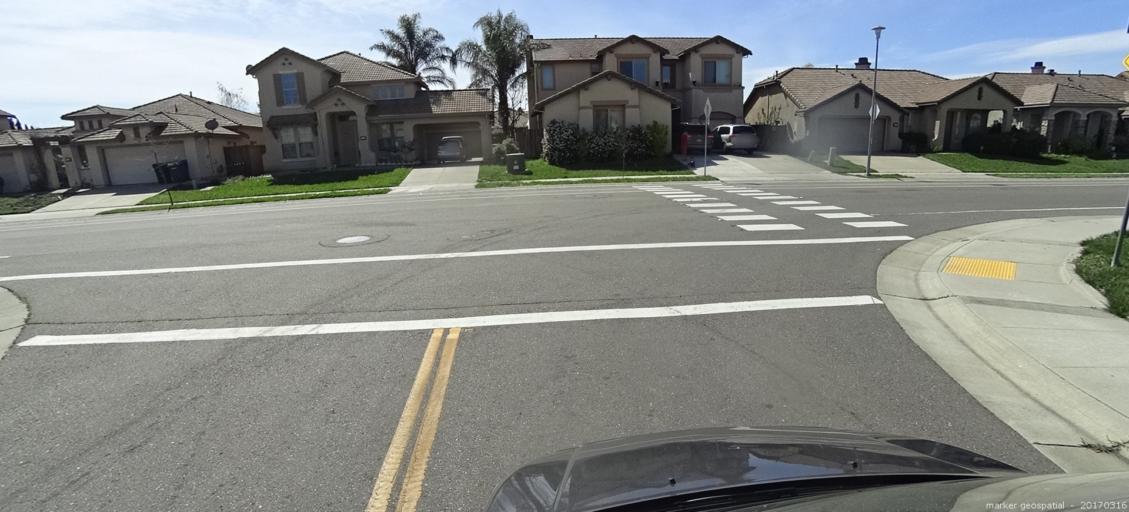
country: US
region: California
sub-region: Sacramento County
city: Parkway
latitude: 38.4752
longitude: -121.4902
